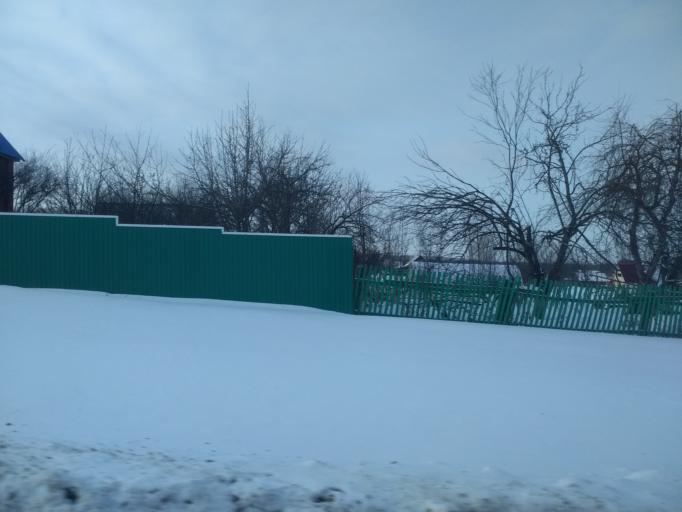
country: RU
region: Bashkortostan
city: Iglino
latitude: 54.7741
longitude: 56.5365
